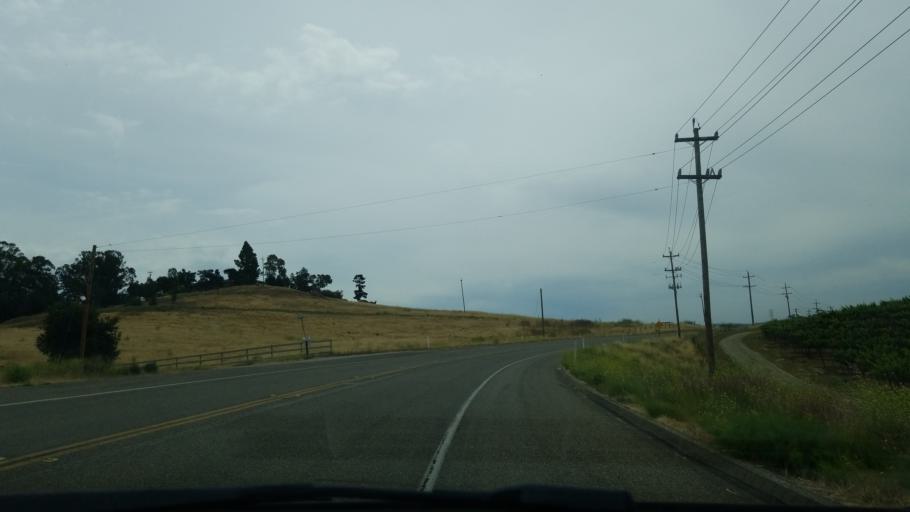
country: US
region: California
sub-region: San Luis Obispo County
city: San Luis Obispo
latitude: 35.2390
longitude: -120.6040
